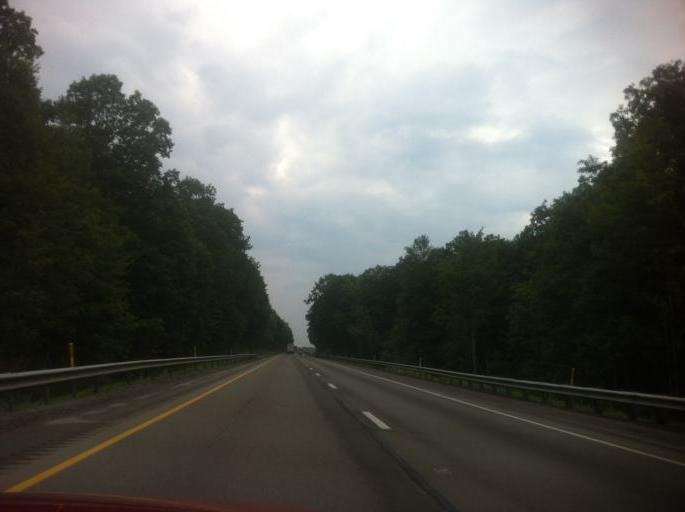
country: US
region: Pennsylvania
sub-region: Jefferson County
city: Brookville
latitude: 41.1802
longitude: -79.1336
